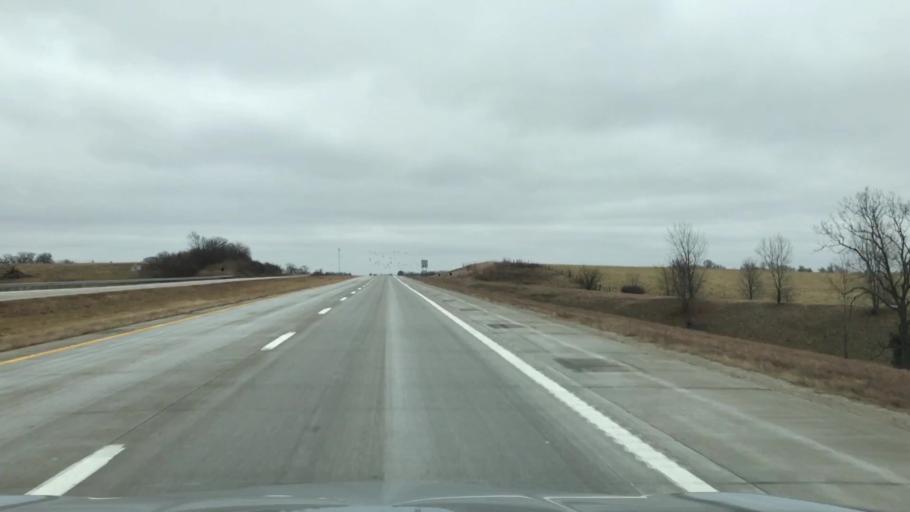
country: US
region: Missouri
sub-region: Caldwell County
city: Hamilton
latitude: 39.7349
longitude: -93.7952
